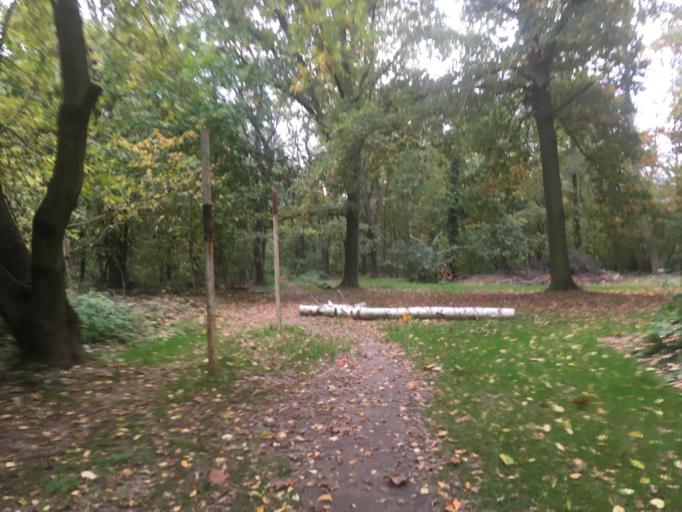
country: DE
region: Berlin
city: Staaken
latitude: 52.5206
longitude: 13.1347
